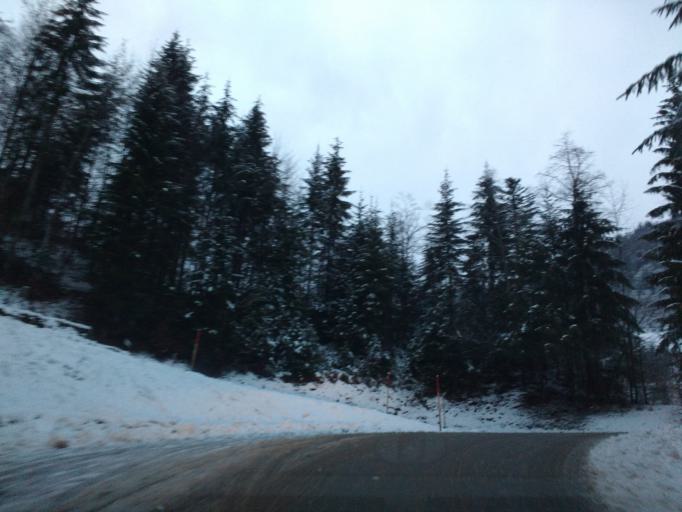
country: DE
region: Bavaria
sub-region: Swabia
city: Obermaiselstein
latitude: 47.4047
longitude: 10.2201
